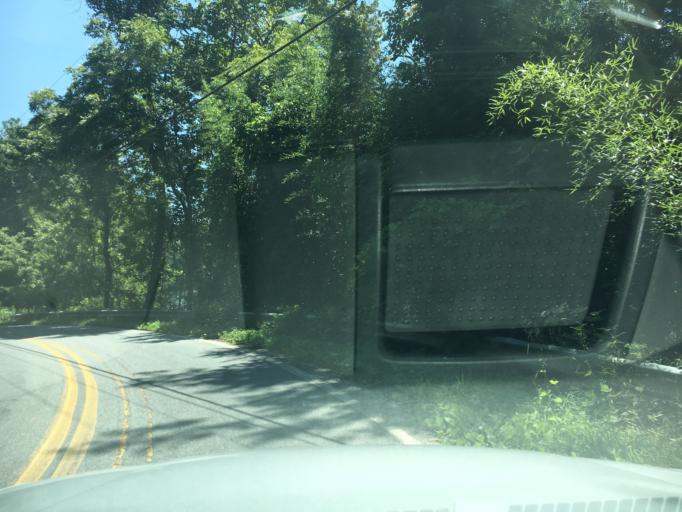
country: US
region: North Carolina
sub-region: McDowell County
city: Marion
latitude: 35.6980
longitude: -82.0464
